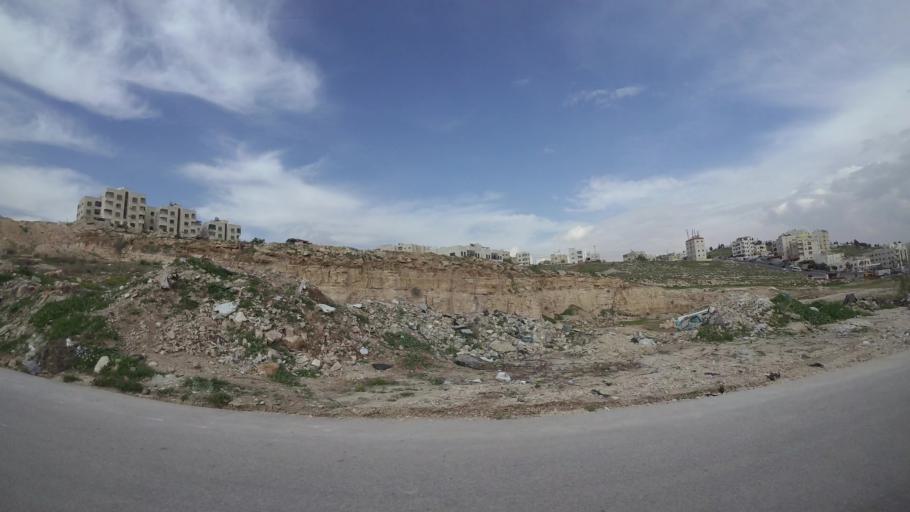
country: JO
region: Amman
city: Amman
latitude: 32.0132
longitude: 35.9485
